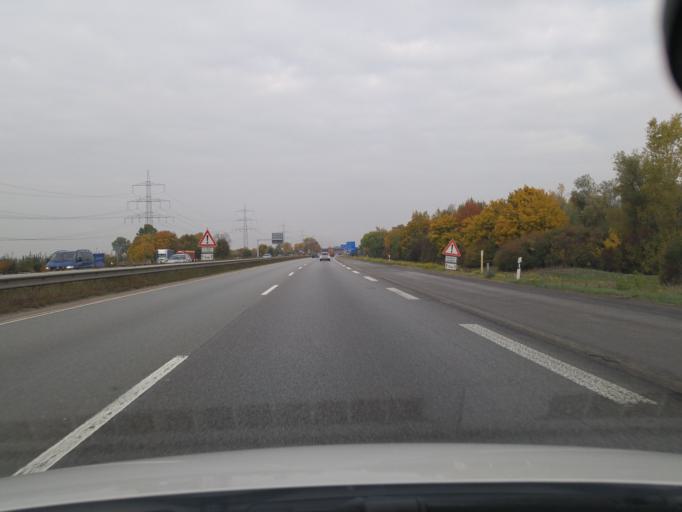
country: DE
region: Rheinland-Pfalz
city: Dannstadt-Schauernheim
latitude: 49.4607
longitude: 8.3146
